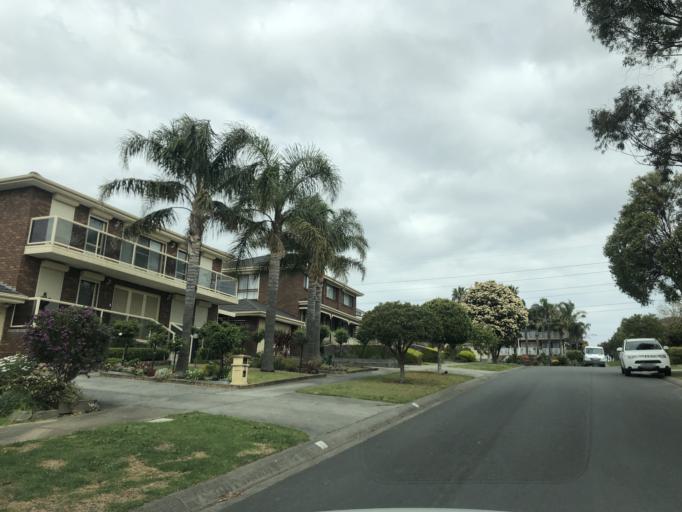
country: AU
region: Victoria
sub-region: Monash
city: Mulgrave
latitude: -37.9292
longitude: 145.1986
